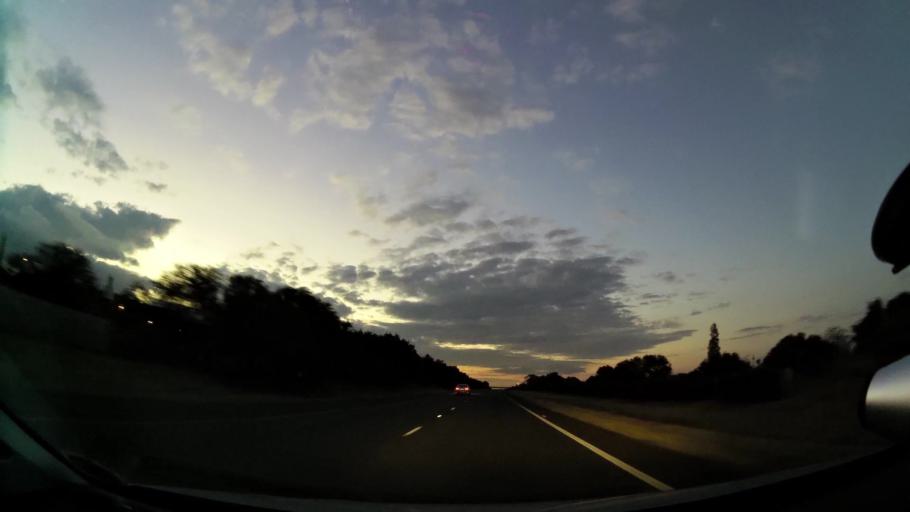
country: ZA
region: Orange Free State
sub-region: Mangaung Metropolitan Municipality
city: Bloemfontein
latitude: -29.1527
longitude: 26.1744
